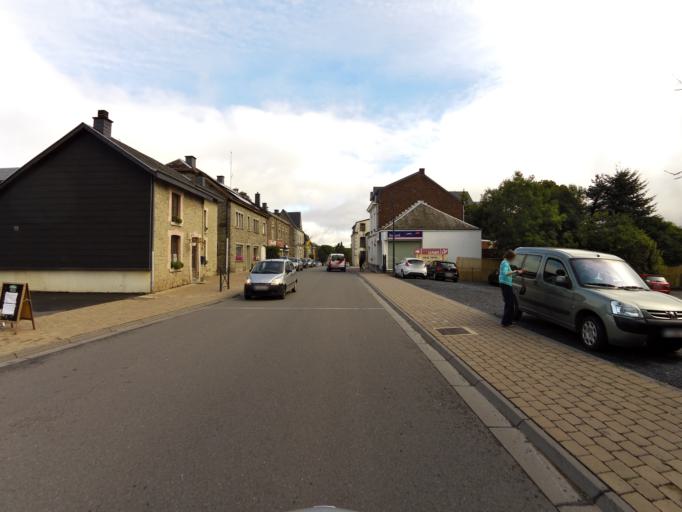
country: BE
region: Wallonia
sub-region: Province du Luxembourg
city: Erezee
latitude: 50.2929
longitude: 5.5580
